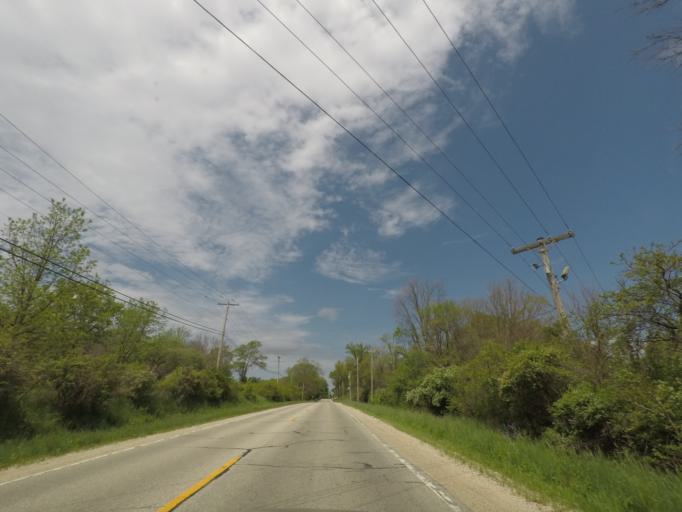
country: US
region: Wisconsin
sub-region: Rock County
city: Beloit
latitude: 42.5264
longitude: -89.0758
